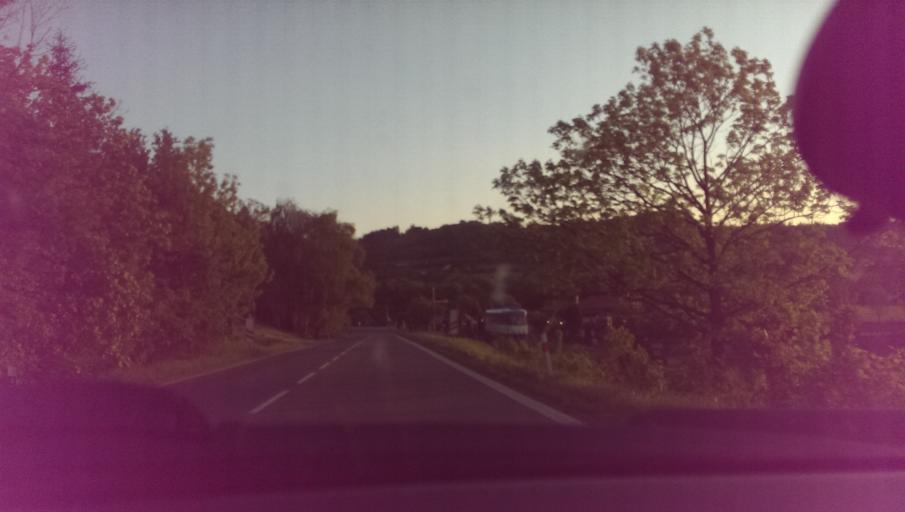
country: CZ
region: Zlin
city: Valasske Mezirici
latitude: 49.4532
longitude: 17.9708
